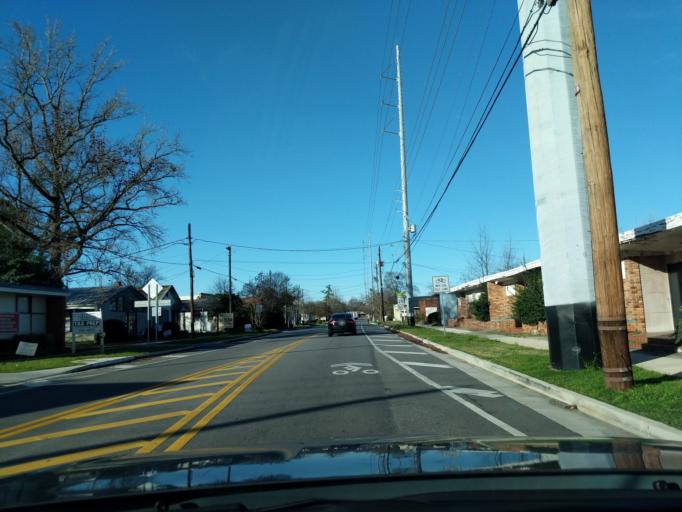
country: US
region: Georgia
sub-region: Richmond County
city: Augusta
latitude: 33.4720
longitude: -81.9964
